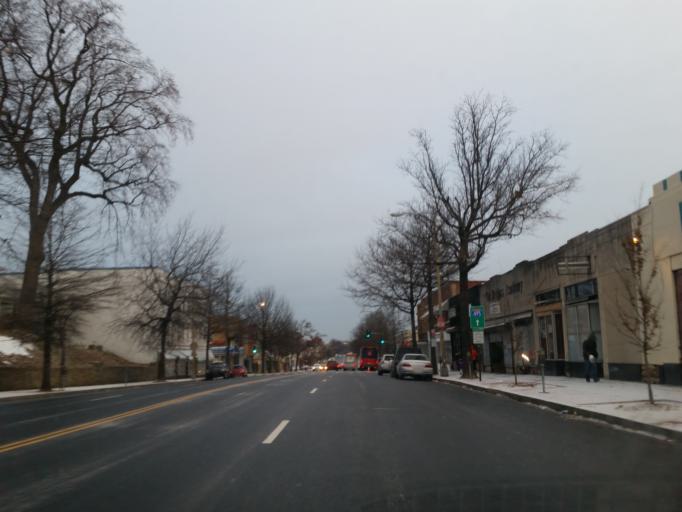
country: US
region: Maryland
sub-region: Montgomery County
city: Takoma Park
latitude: 38.9640
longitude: -77.0277
